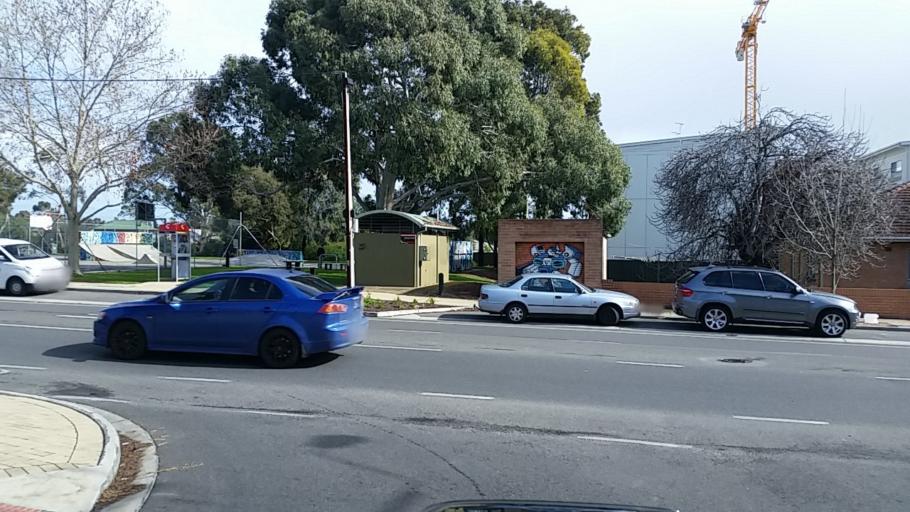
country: AU
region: South Australia
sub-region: Prospect
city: Prospect
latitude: -34.8928
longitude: 138.5855
